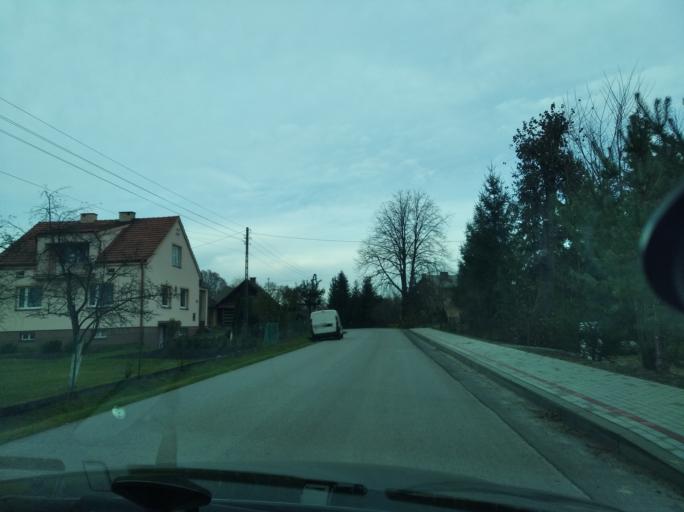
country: PL
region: Subcarpathian Voivodeship
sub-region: Powiat przeworski
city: Grzeska
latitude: 50.0881
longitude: 22.4460
